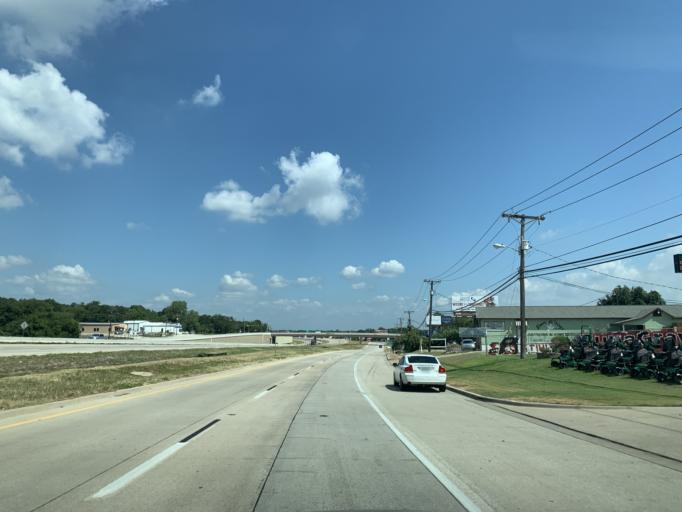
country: US
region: Texas
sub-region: Tarrant County
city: Azle
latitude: 32.8635
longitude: -97.5224
